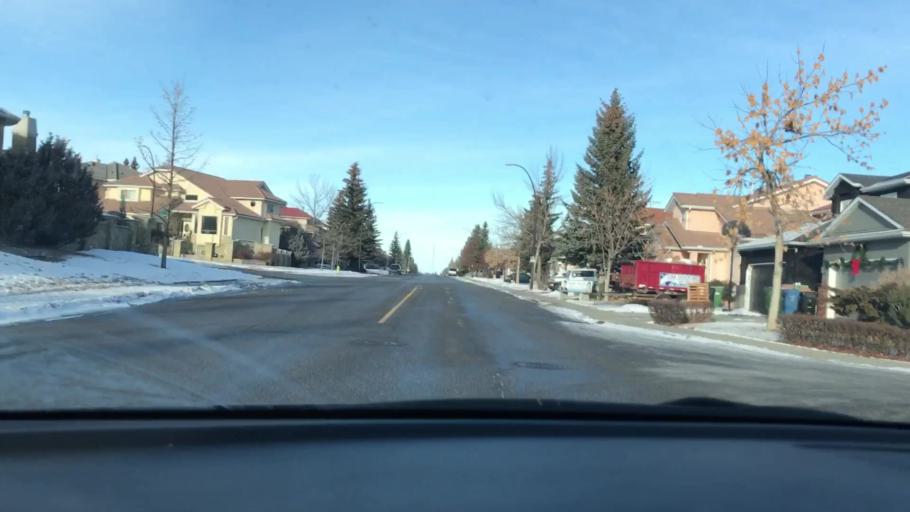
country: CA
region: Alberta
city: Calgary
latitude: 51.0242
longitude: -114.1702
